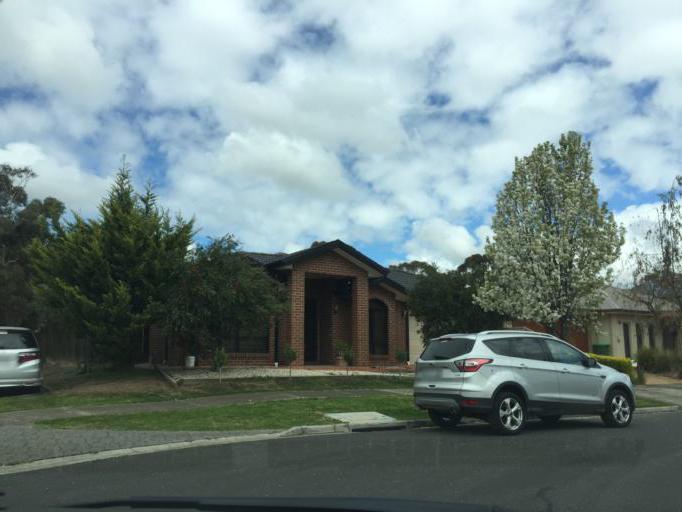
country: AU
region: Victoria
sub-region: Maribyrnong
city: Braybrook
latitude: -37.7960
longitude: 144.8538
